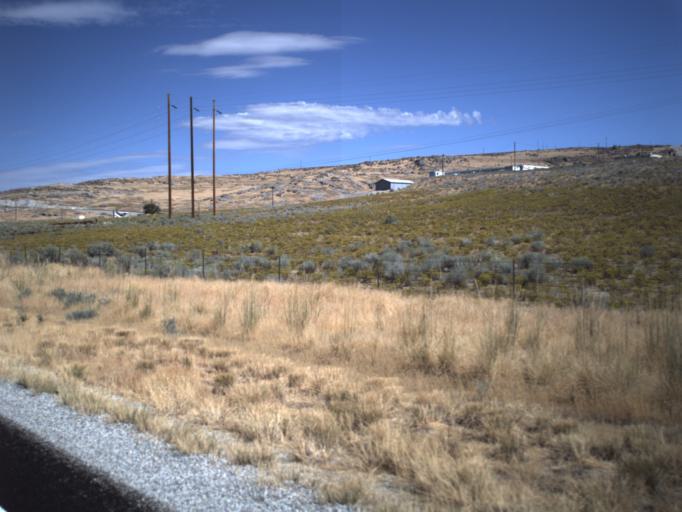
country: US
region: Utah
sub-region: Box Elder County
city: Tremonton
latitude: 41.6335
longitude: -112.4209
